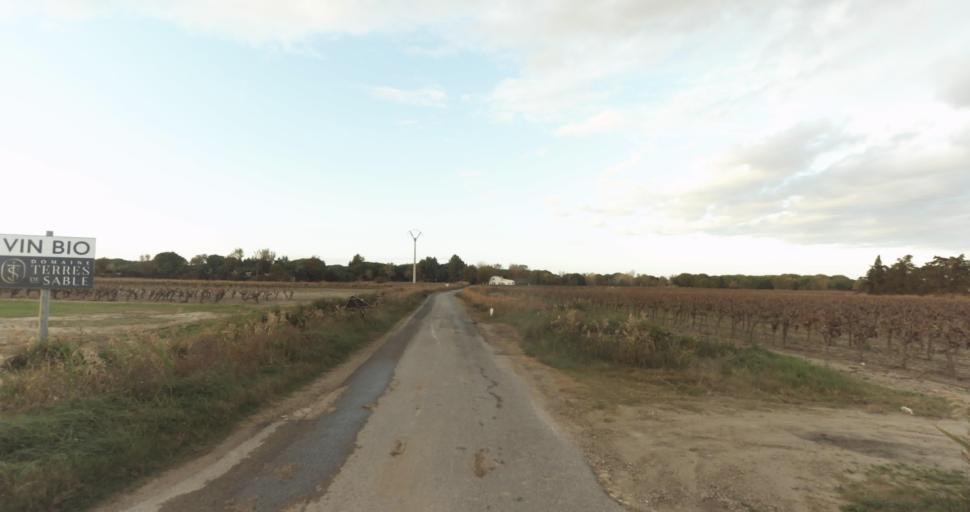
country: FR
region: Languedoc-Roussillon
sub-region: Departement du Gard
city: Aigues-Mortes
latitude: 43.5789
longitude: 4.1867
